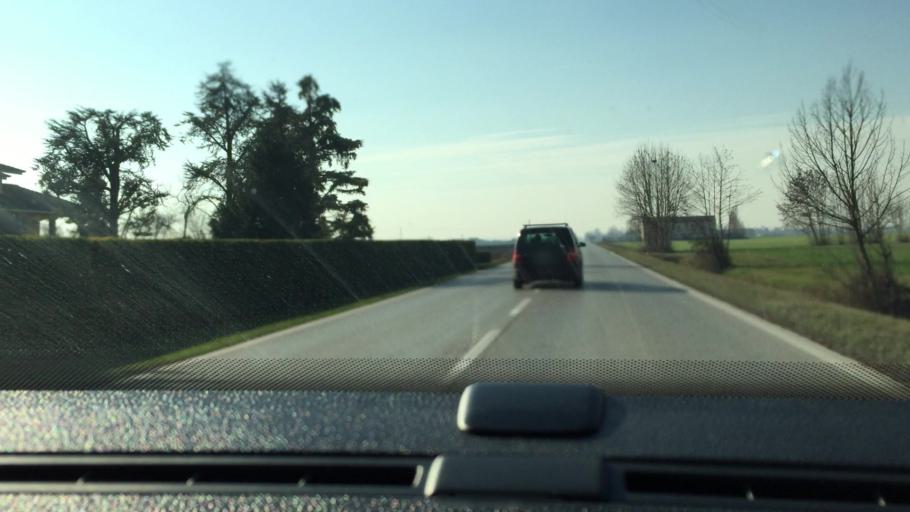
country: IT
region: Lombardy
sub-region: Provincia di Mantova
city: Rodigo
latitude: 45.2309
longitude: 10.6324
